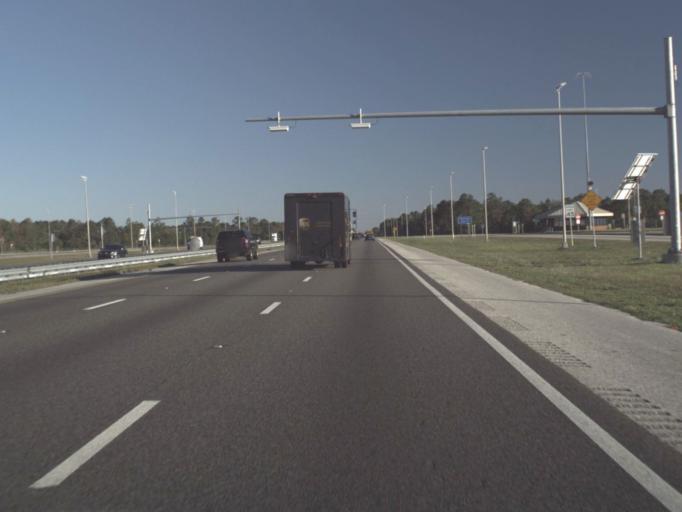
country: US
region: Florida
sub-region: Flagler County
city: Palm Coast
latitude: 29.5119
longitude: -81.1977
